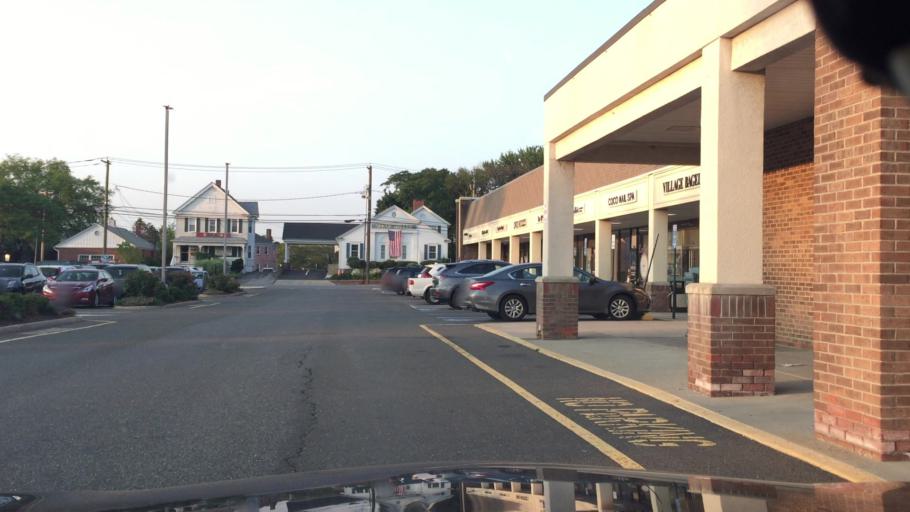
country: US
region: Connecticut
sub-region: Fairfield County
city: Fairfield
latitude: 41.1462
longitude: -73.2493
